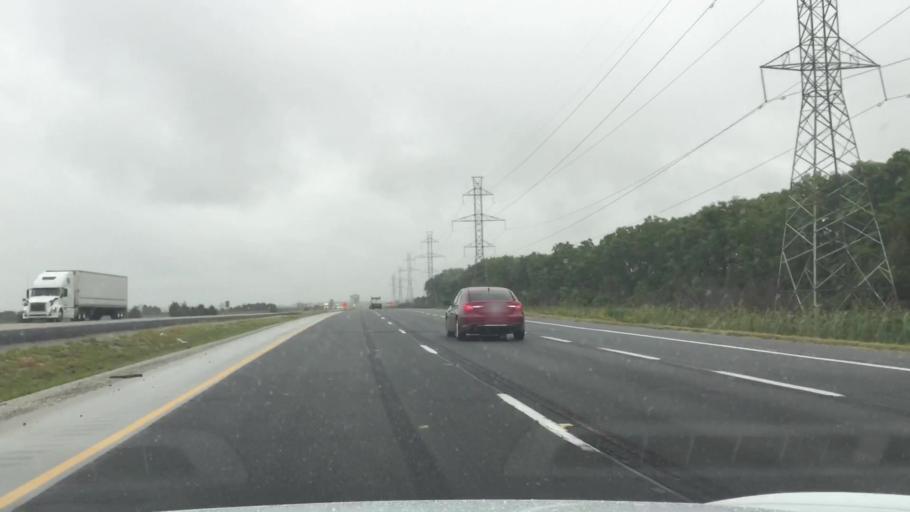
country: CA
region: Ontario
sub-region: Lambton County
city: Walpole Island
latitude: 42.3540
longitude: -82.1794
